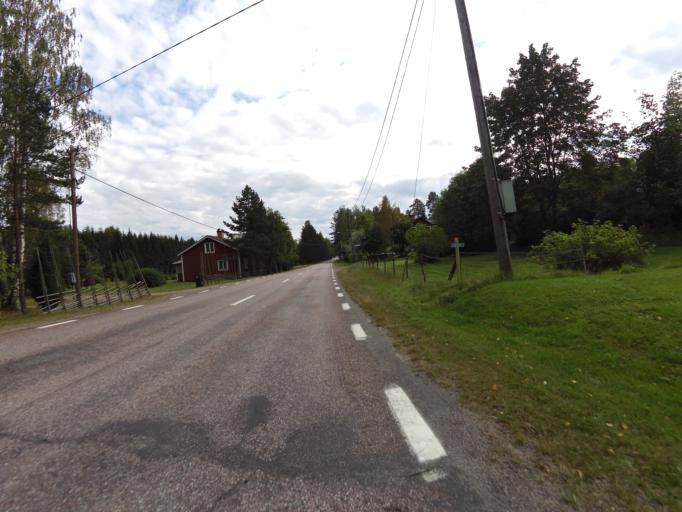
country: SE
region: Gaevleborg
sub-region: Sandvikens Kommun
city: Sandviken
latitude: 60.7119
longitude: 16.8070
